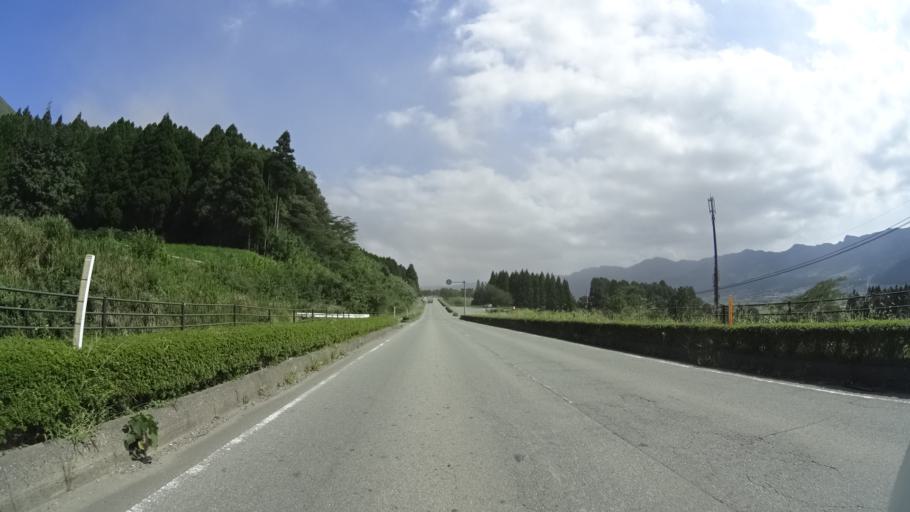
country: JP
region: Kumamoto
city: Aso
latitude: 32.8489
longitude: 131.0280
